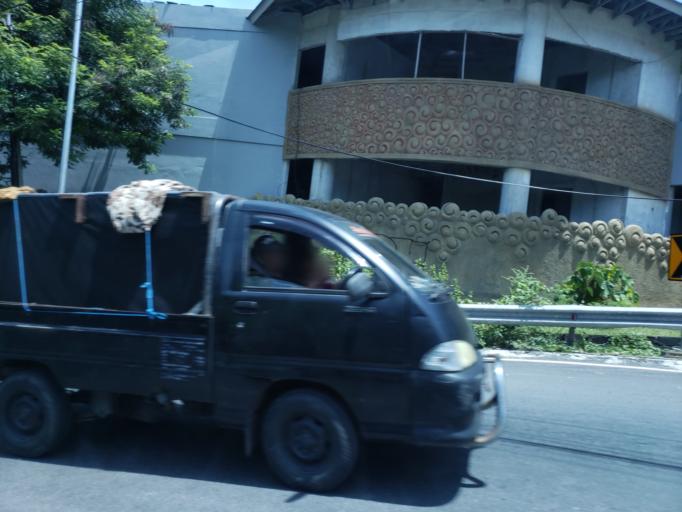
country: ID
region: Bali
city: Jimbaran
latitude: -8.7863
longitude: 115.1665
